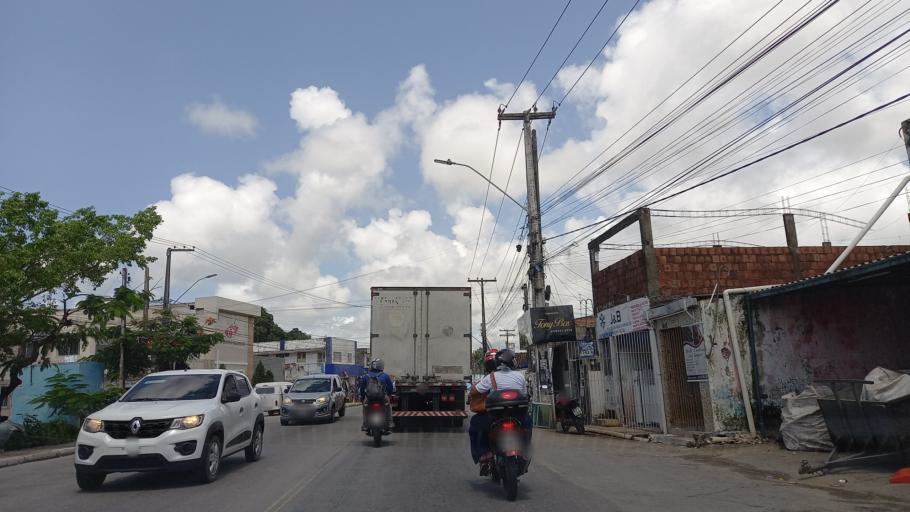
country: BR
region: Pernambuco
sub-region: Jaboatao Dos Guararapes
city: Jaboatao
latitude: -8.2242
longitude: -34.9669
